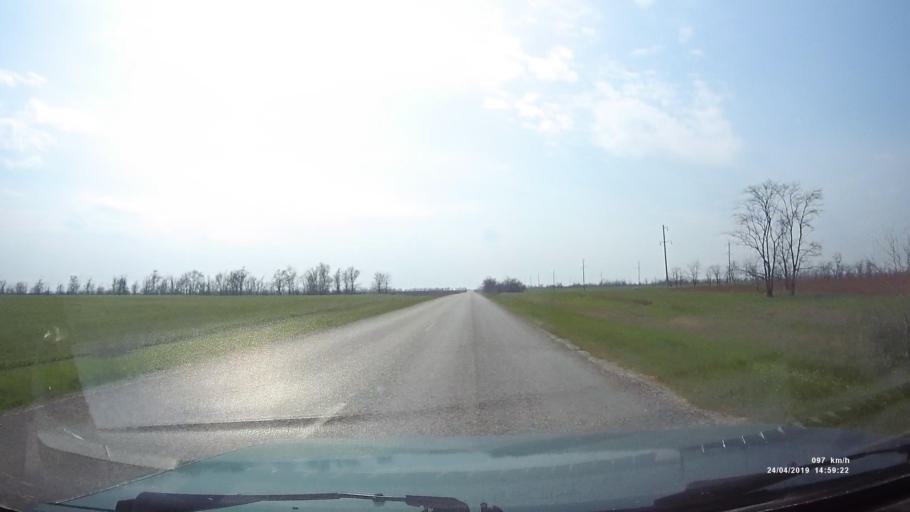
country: RU
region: Rostov
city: Remontnoye
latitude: 46.5662
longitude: 43.5792
